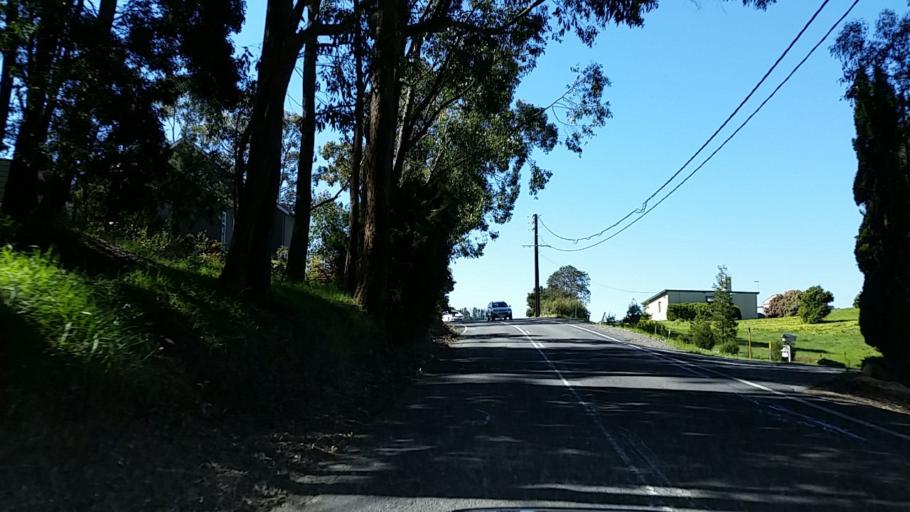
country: AU
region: South Australia
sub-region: Adelaide Hills
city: Bridgewater
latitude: -34.9749
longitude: 138.7302
